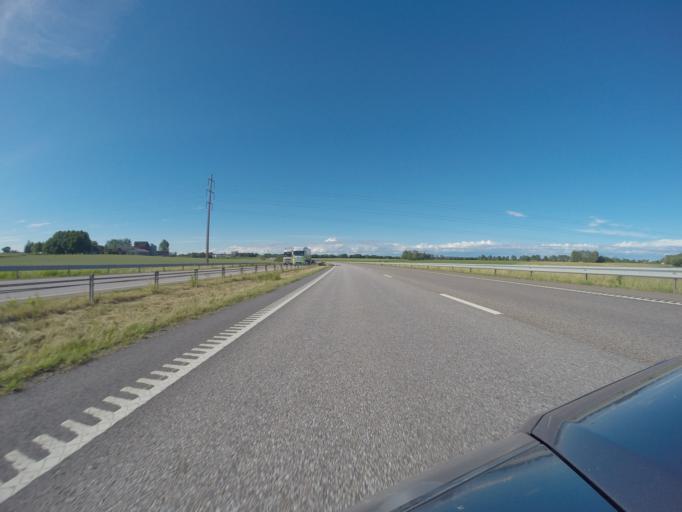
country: SE
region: Skane
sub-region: Angelholms Kommun
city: Strovelstorp
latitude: 56.1426
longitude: 12.8431
